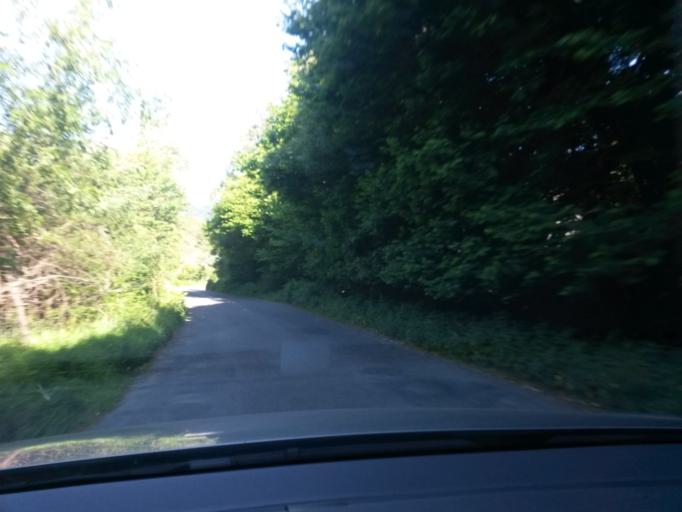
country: IE
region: Leinster
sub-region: Wicklow
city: Rathdrum
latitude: 53.0334
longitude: -6.3162
